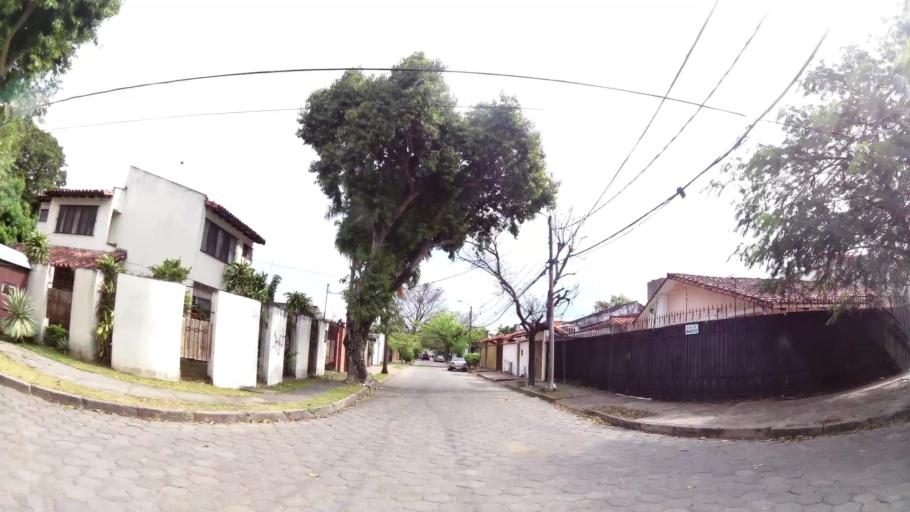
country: BO
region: Santa Cruz
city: Santa Cruz de la Sierra
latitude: -17.7936
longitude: -63.2008
